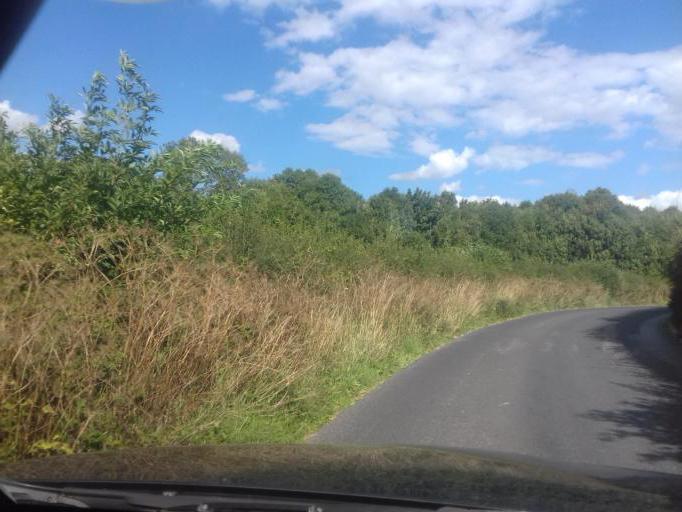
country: IE
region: Leinster
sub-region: Kilkenny
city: Kilkenny
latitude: 52.5391
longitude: -7.2540
